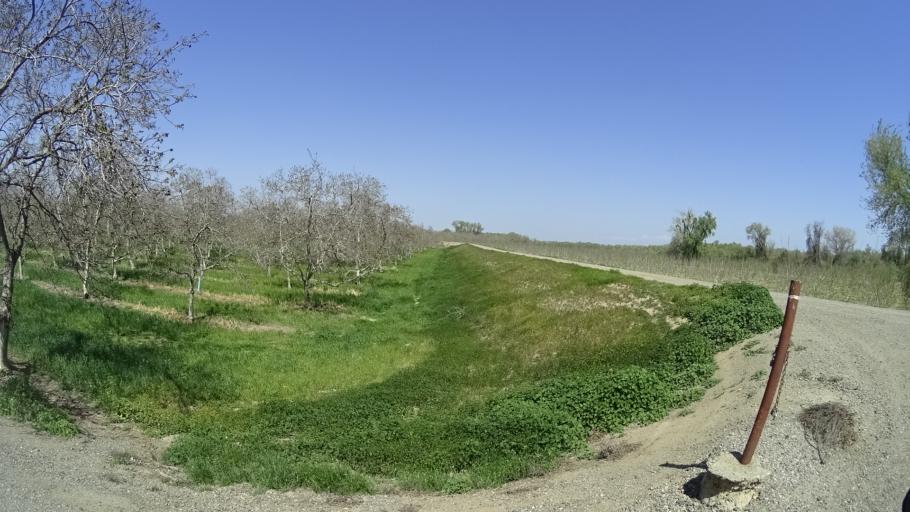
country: US
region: California
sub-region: Glenn County
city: Willows
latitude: 39.5108
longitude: -122.0094
